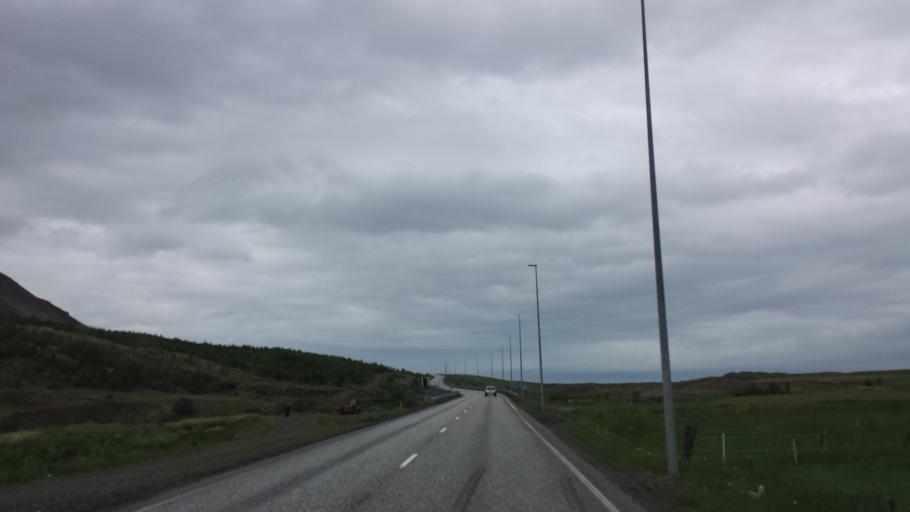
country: IS
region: Capital Region
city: Mosfellsbaer
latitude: 64.1803
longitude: -21.6410
